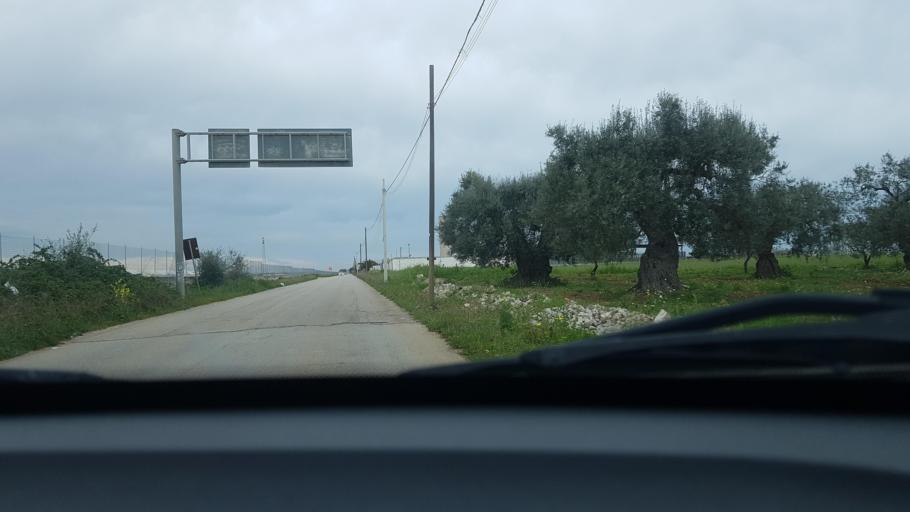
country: IT
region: Apulia
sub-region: Provincia di Bari
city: Noicattaro
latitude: 41.0341
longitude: 16.9762
